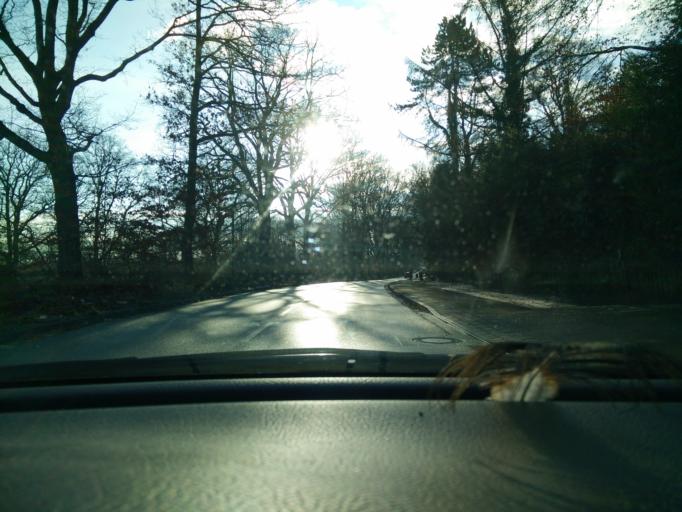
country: DE
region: Hamburg
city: Lemsahl-Mellingstedt
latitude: 53.6851
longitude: 10.0951
